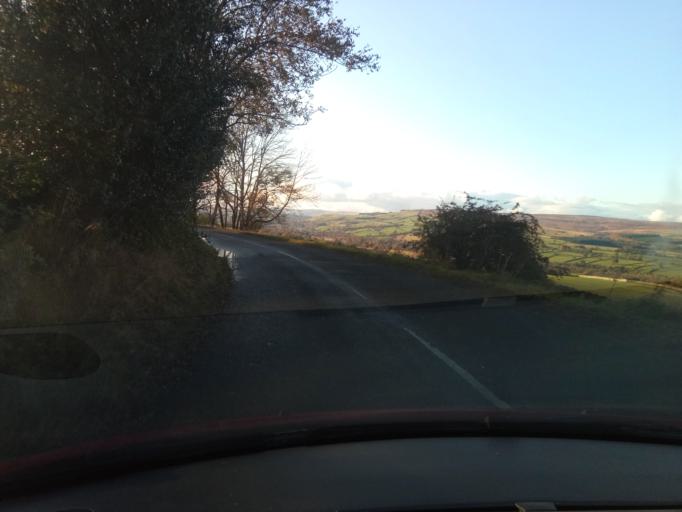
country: GB
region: England
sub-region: County Durham
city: Wolsingham
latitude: 54.7167
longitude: -1.8866
